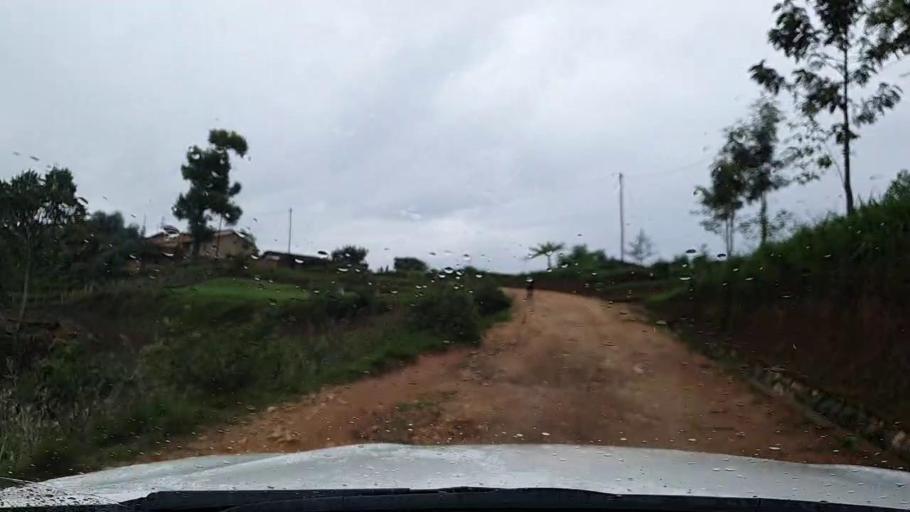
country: RW
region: Southern Province
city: Nzega
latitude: -2.4683
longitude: 29.4972
